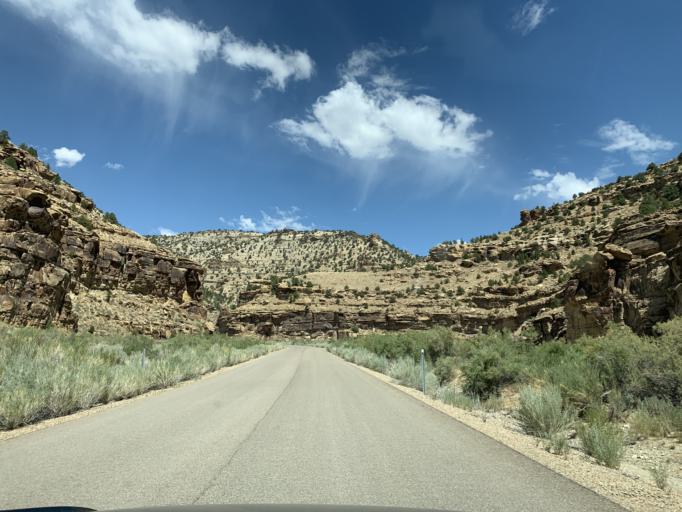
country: US
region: Utah
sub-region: Carbon County
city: East Carbon City
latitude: 39.8145
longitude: -110.2511
